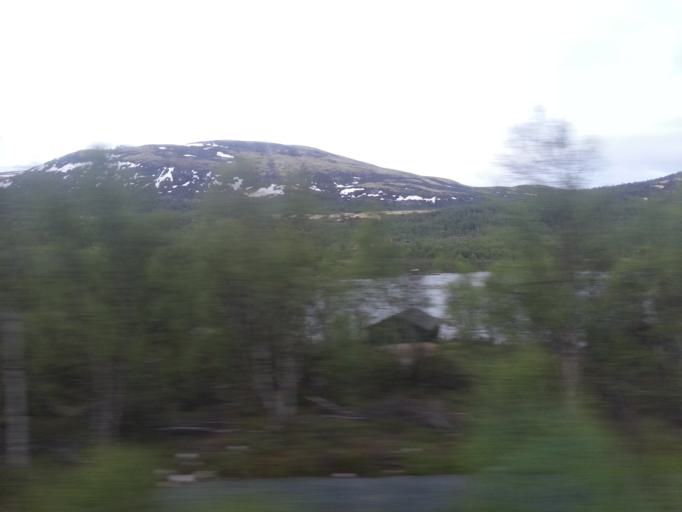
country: NO
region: Oppland
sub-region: Dovre
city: Dovre
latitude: 62.1763
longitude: 9.4234
